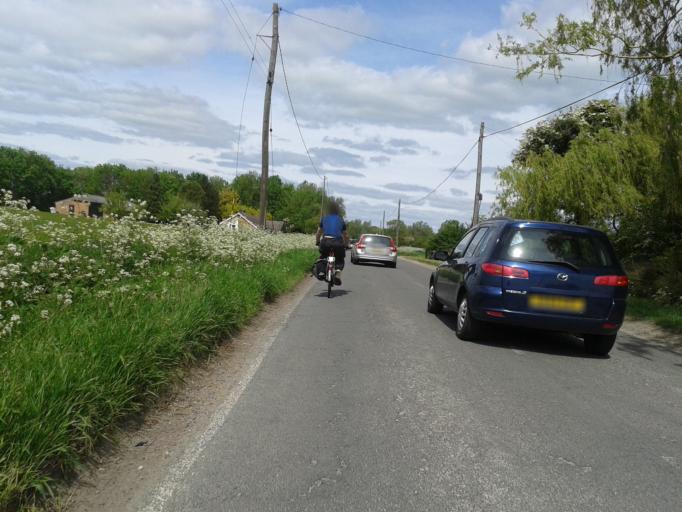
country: GB
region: England
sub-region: Cambridgeshire
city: Meldreth
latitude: 52.1180
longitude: 0.0262
